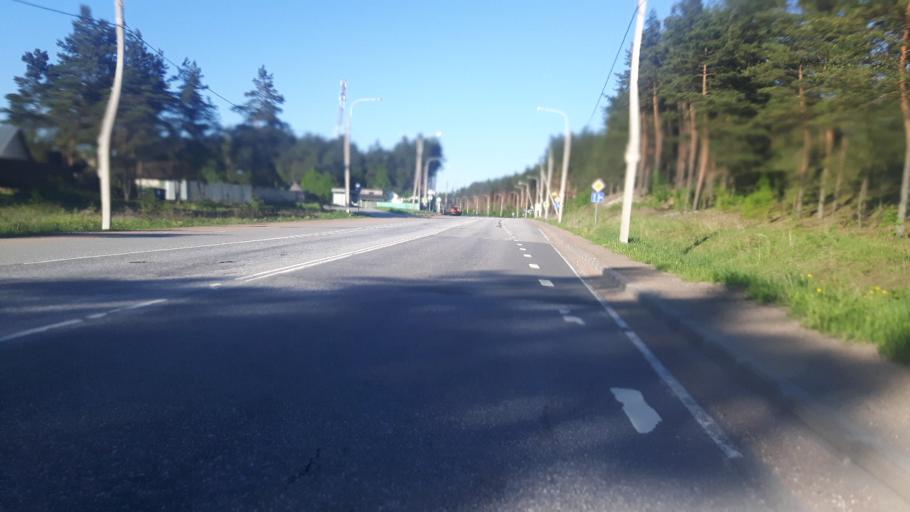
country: RU
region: Leningrad
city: Molodezhnoye
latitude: 60.1689
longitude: 29.4244
